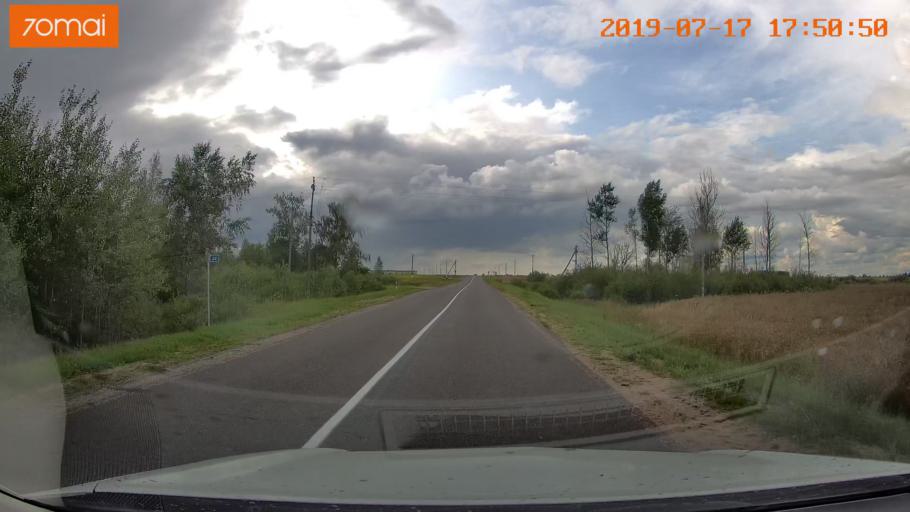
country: BY
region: Mogilev
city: Hlusha
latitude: 53.1456
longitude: 28.7964
